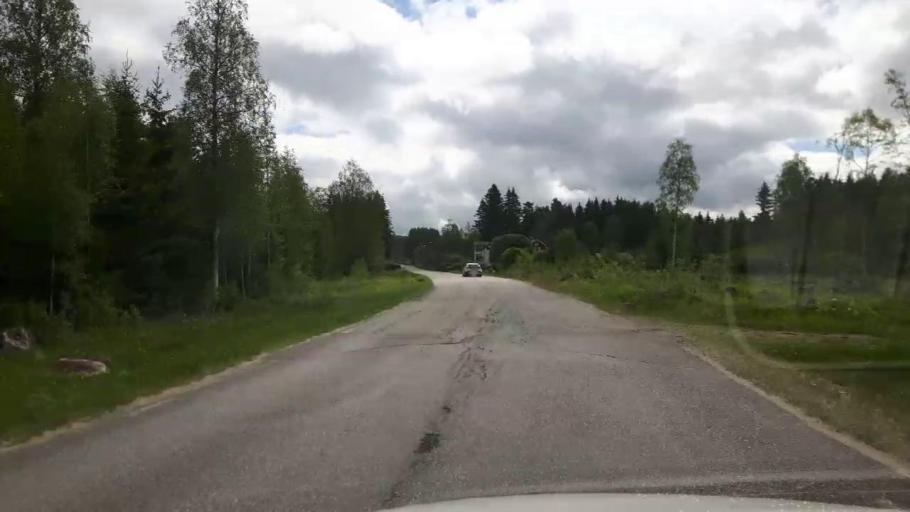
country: SE
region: Gaevleborg
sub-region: Ovanakers Kommun
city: Edsbyn
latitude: 61.3414
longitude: 15.9394
